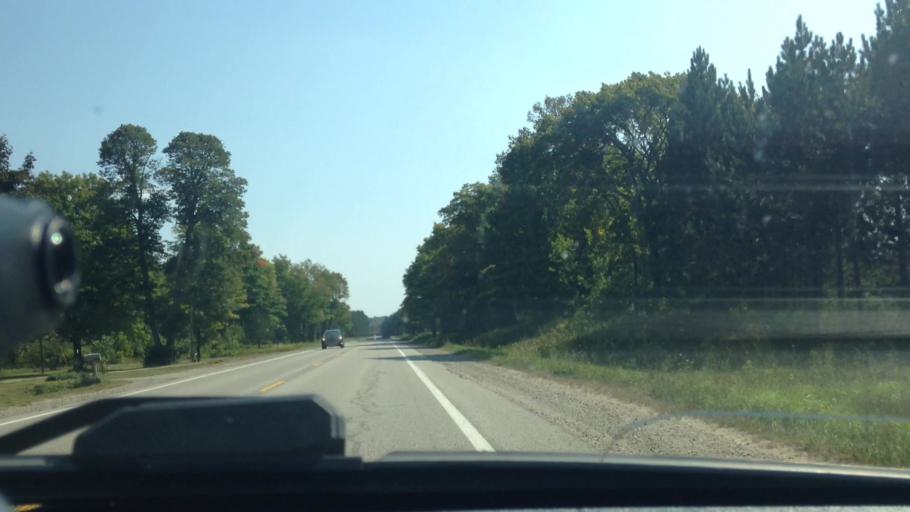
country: US
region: Michigan
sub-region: Luce County
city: Newberry
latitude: 46.3199
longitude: -85.6669
